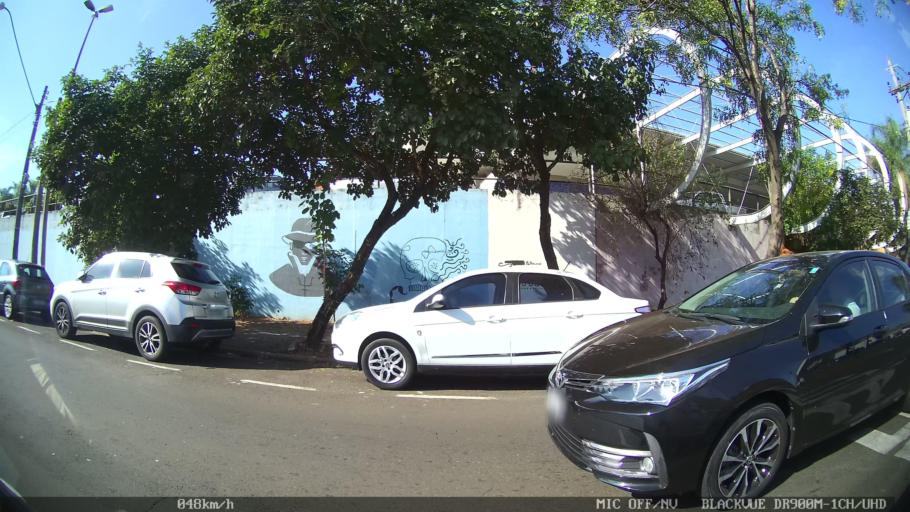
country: BR
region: Sao Paulo
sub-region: Sao Jose Do Rio Preto
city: Sao Jose do Rio Preto
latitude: -20.8117
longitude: -49.4046
